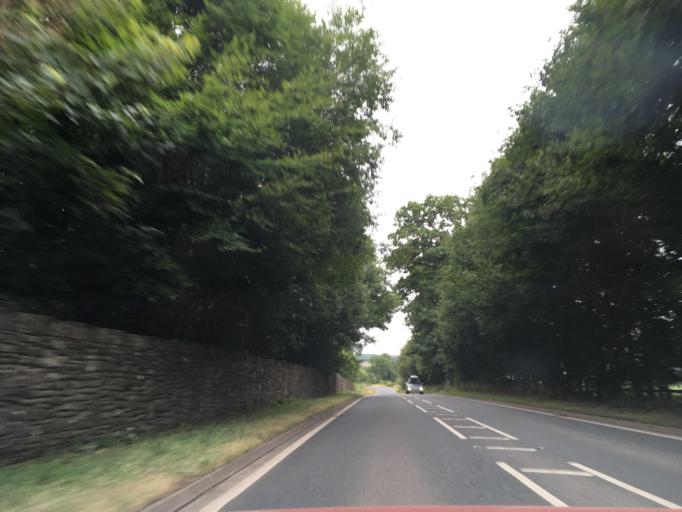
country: GB
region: Wales
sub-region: Blaenau Gwent
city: Brynmawr
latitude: 51.8760
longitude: -3.1811
